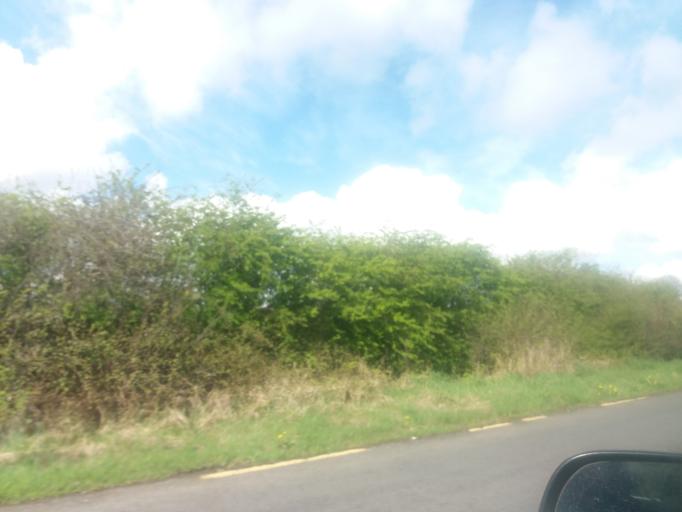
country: IE
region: Ulster
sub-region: An Cabhan
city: Belturbet
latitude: 54.1178
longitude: -7.4794
